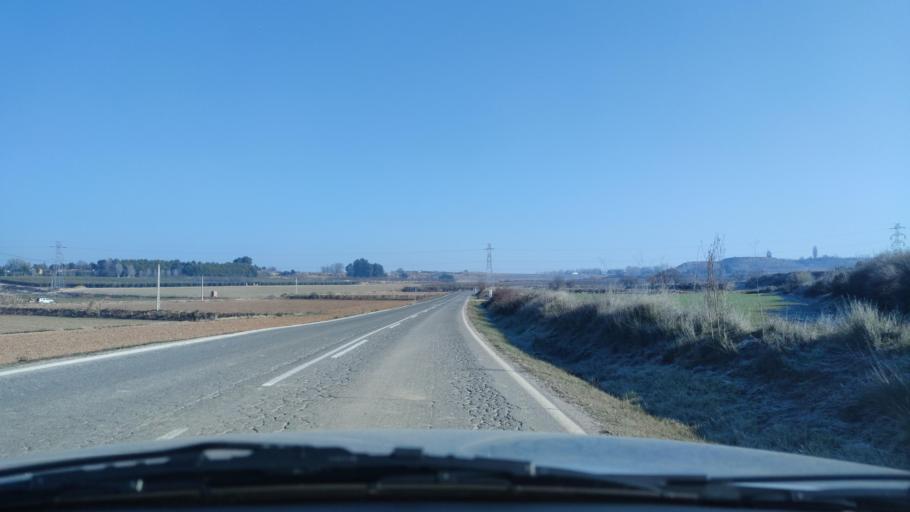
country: ES
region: Catalonia
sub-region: Provincia de Lleida
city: Juneda
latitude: 41.5698
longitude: 0.7535
